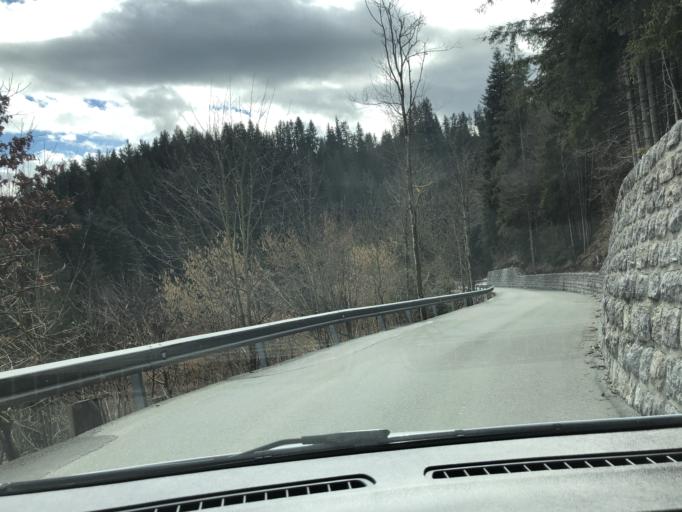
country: AT
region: Tyrol
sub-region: Politischer Bezirk Kitzbuhel
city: Hopfgarten im Brixental
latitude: 47.4477
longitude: 12.1508
